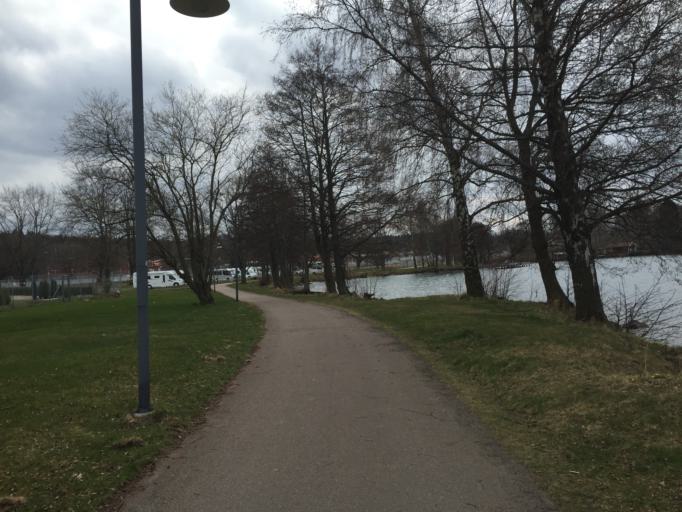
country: SE
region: OEstergoetland
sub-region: Motala Kommun
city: Motala
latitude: 58.5311
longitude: 15.0389
